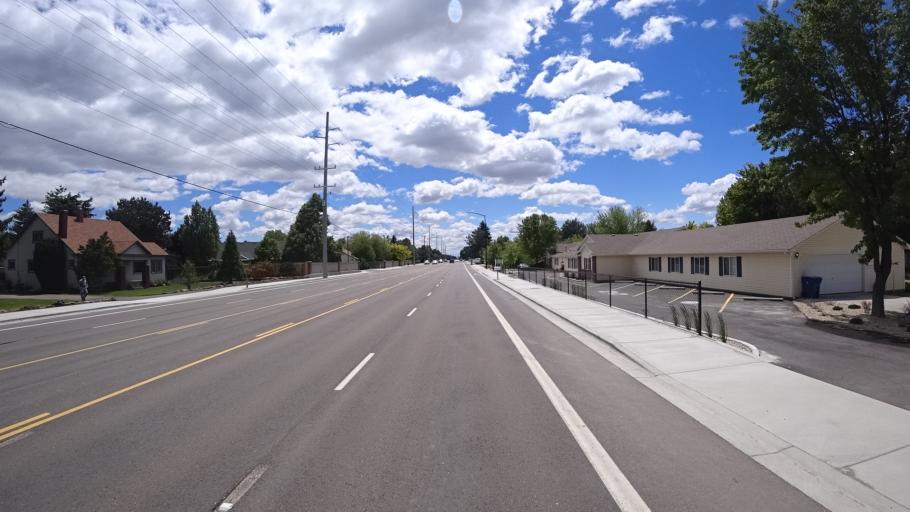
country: US
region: Idaho
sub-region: Ada County
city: Eagle
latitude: 43.6394
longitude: -116.3343
